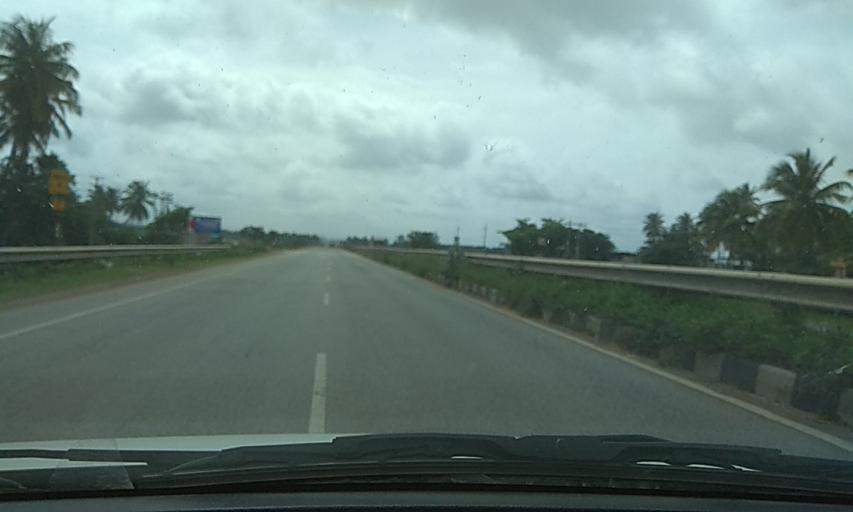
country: IN
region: Karnataka
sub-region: Davanagere
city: Harihar
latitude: 14.4512
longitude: 75.8764
